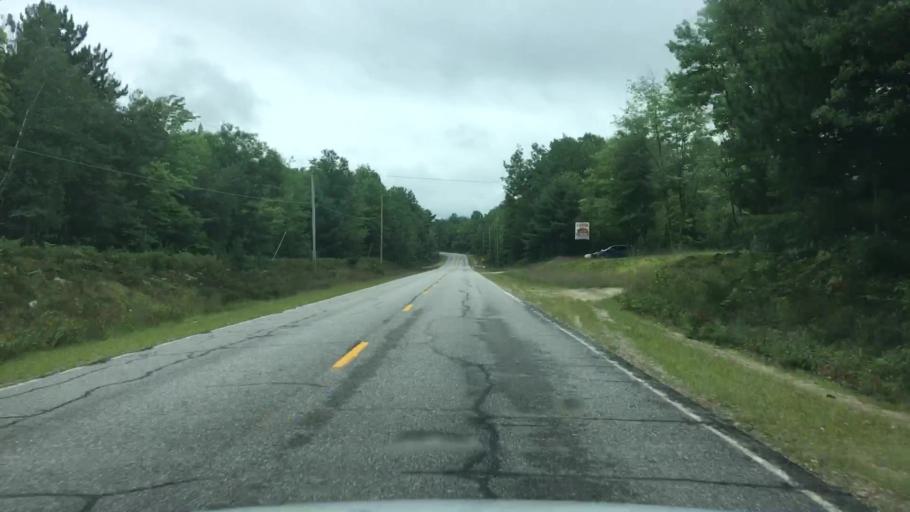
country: US
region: Maine
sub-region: Oxford County
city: Brownfield
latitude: 43.9354
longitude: -70.8847
